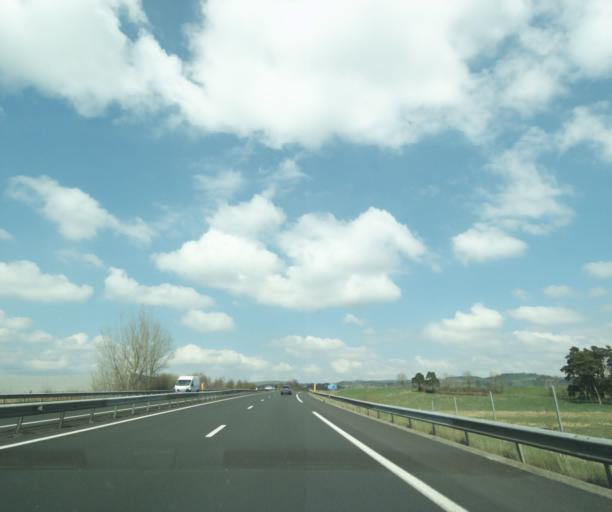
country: FR
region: Auvergne
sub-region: Departement du Cantal
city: Saint-Flour
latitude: 45.0613
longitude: 3.1106
